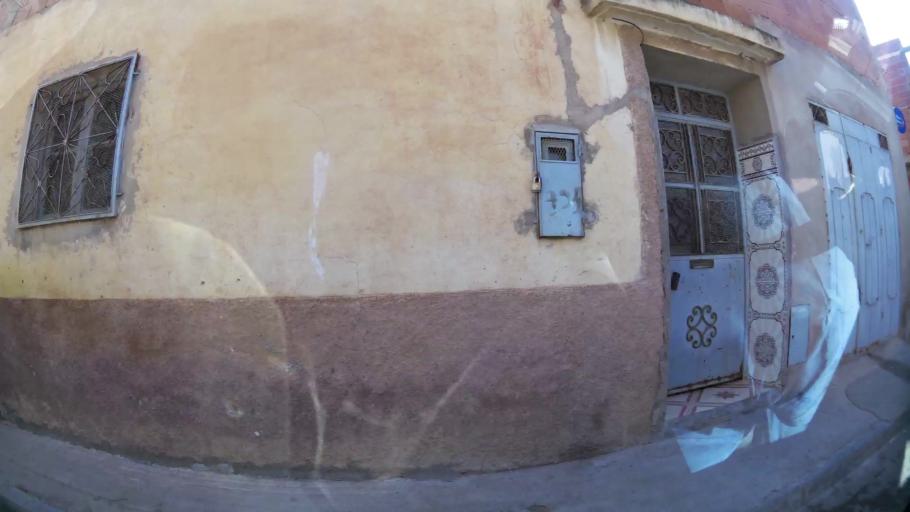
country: MA
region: Oriental
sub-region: Oujda-Angad
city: Oujda
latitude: 34.7203
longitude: -1.8843
